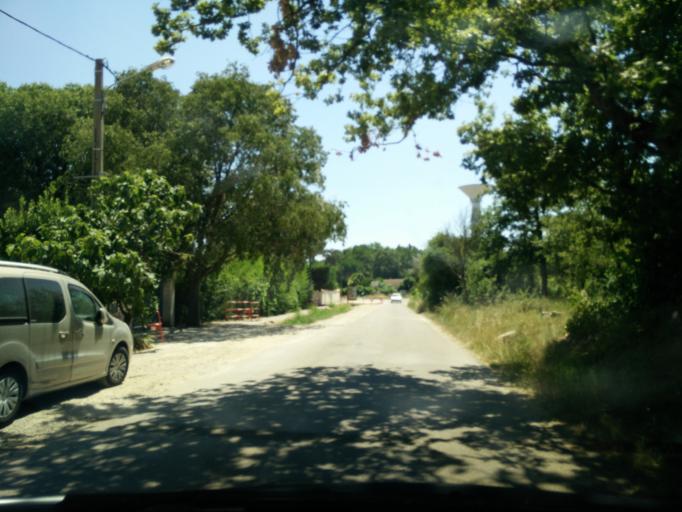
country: FR
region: Languedoc-Roussillon
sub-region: Departement de l'Herault
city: Saint-Christol
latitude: 43.7246
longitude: 4.0748
